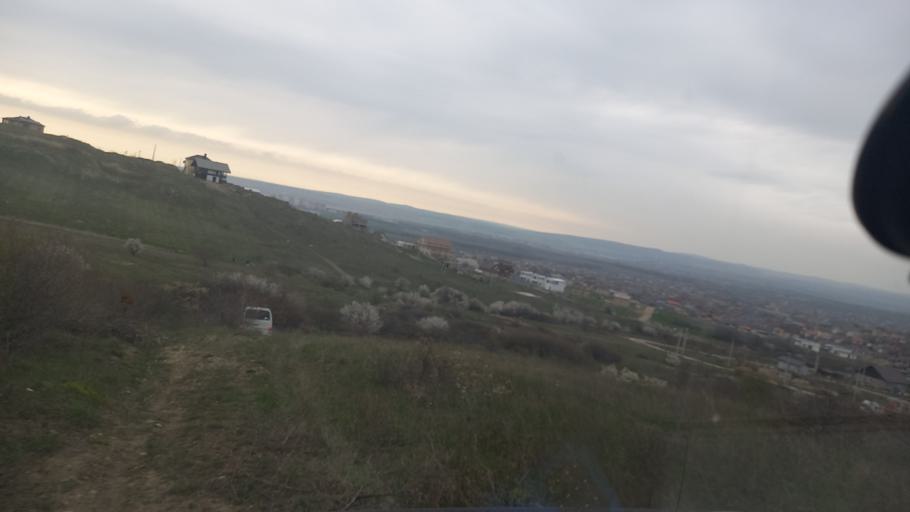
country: RU
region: Krasnodarskiy
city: Anapa
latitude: 44.8521
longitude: 37.3434
